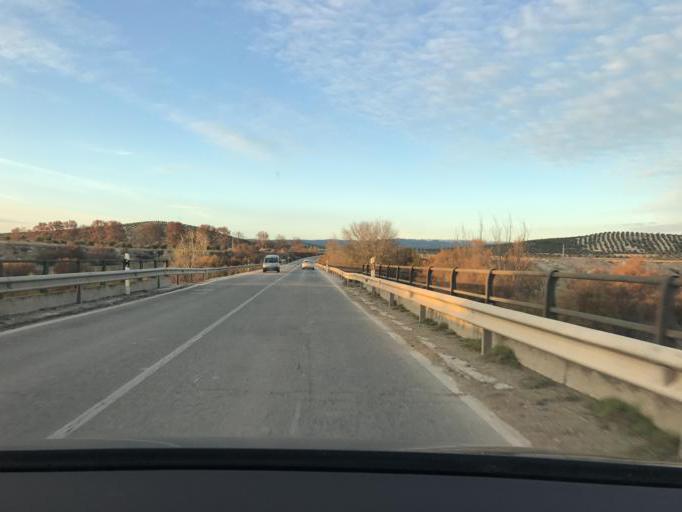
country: ES
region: Andalusia
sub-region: Provincia de Jaen
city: Jodar
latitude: 37.9187
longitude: -3.3505
